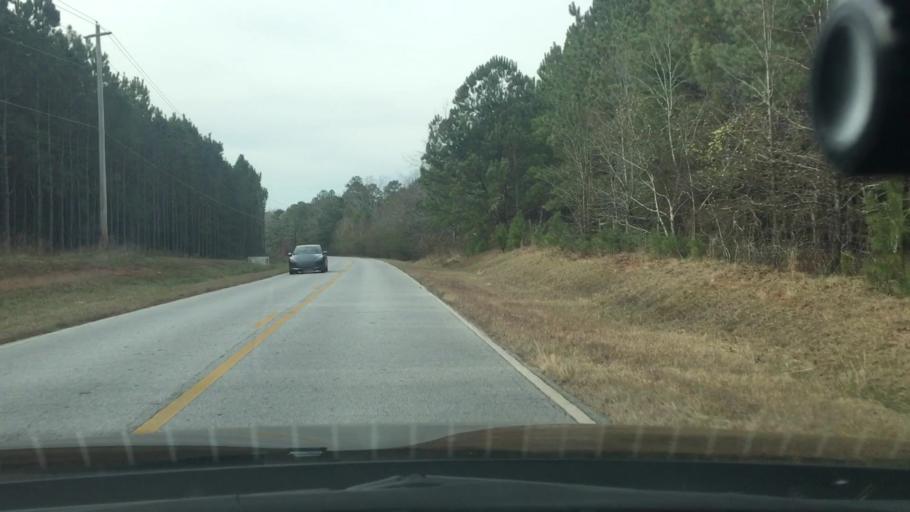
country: US
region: Georgia
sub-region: Spalding County
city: Experiment
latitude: 33.2719
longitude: -84.3504
